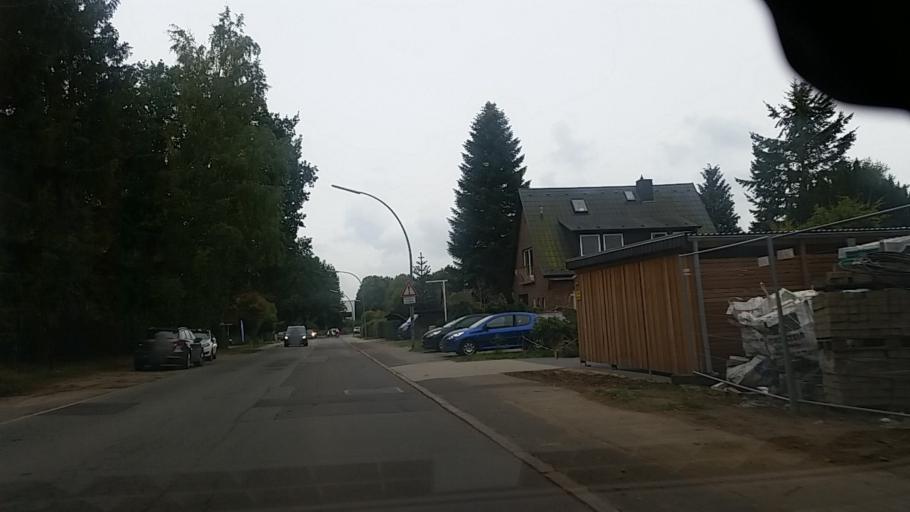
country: DE
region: Hamburg
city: Hummelsbuettel
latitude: 53.6897
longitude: 10.0474
